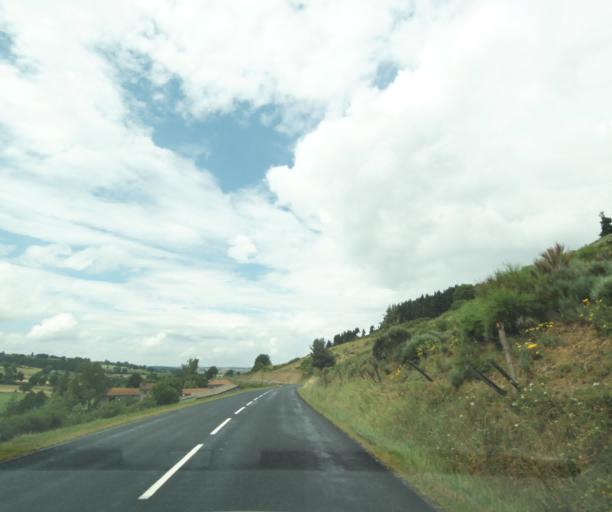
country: FR
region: Auvergne
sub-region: Departement de la Haute-Loire
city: Saugues
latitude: 44.9252
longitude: 3.5435
